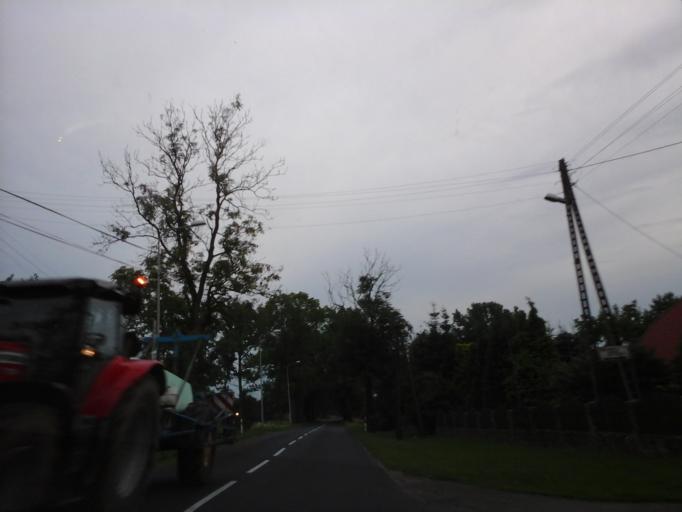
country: PL
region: West Pomeranian Voivodeship
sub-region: Powiat goleniowski
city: Maszewo
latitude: 53.5471
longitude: 15.1248
